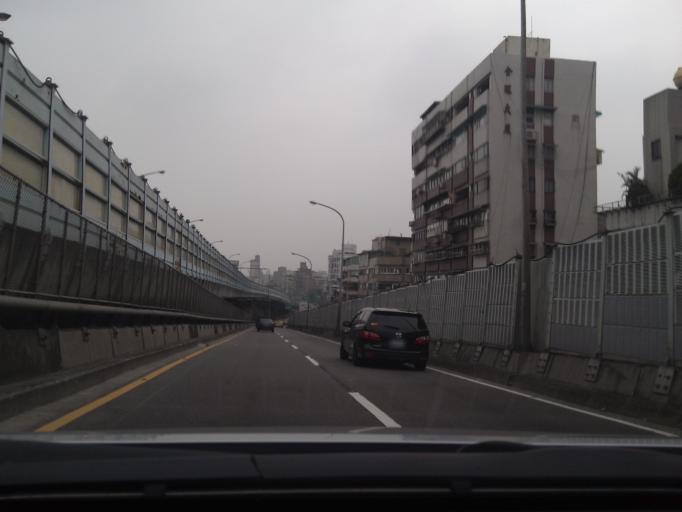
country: TW
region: Taipei
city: Taipei
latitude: 25.0529
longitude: 121.5073
